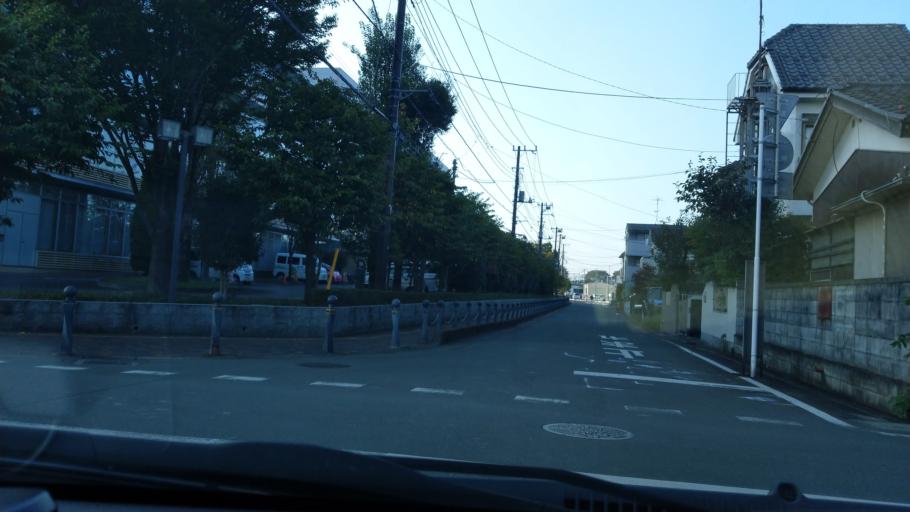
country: JP
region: Saitama
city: Yono
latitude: 35.8559
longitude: 139.6111
